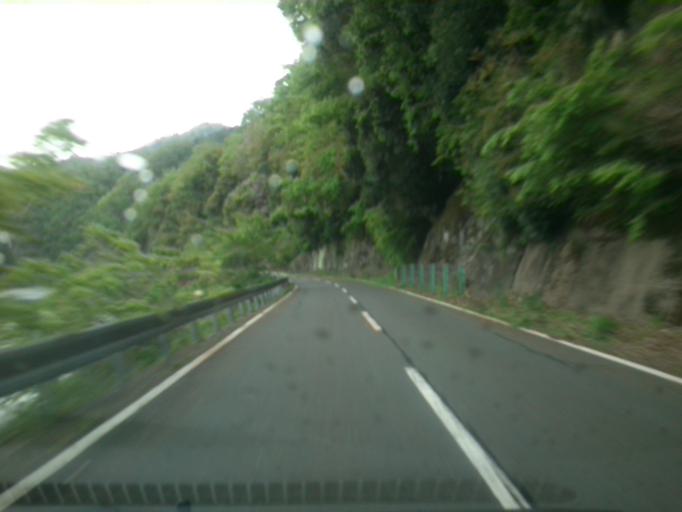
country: JP
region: Kyoto
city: Ayabe
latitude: 35.2758
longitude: 135.3630
